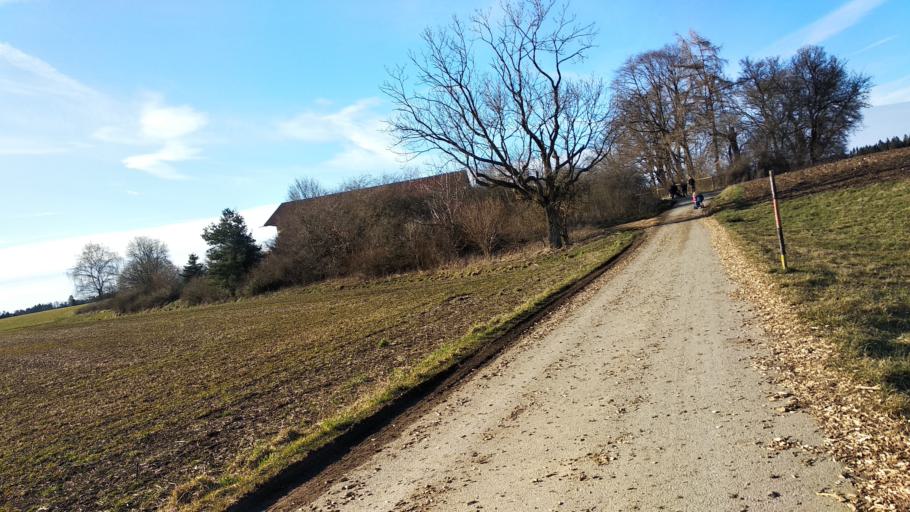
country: DE
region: Bavaria
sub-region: Upper Bavaria
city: Aying
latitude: 47.9798
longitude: 11.7722
